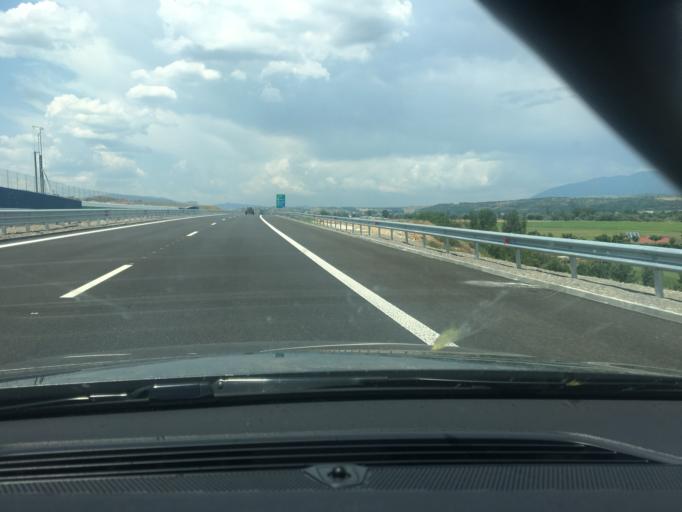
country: BG
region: Blagoevgrad
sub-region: Obshtina Blagoevgrad
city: Blagoevgrad
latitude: 41.9934
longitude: 23.0536
